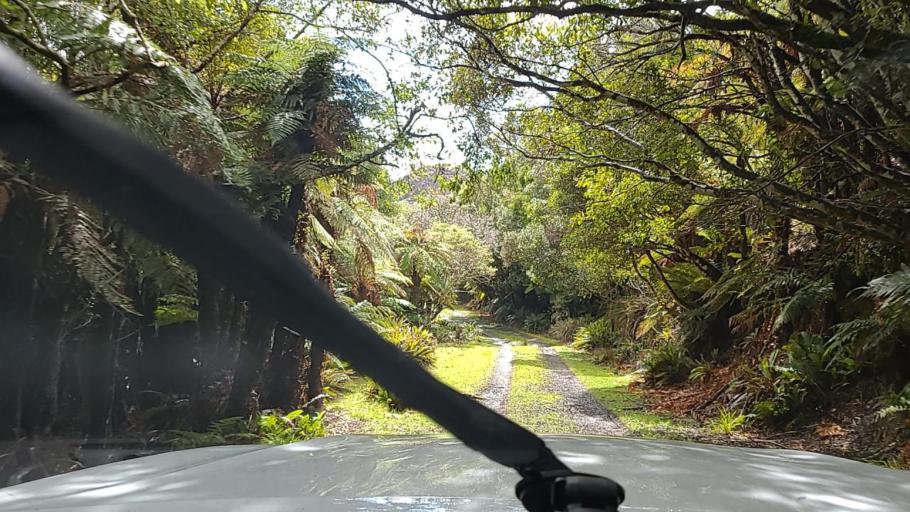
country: NZ
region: Bay of Plenty
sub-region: Opotiki District
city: Opotiki
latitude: -38.2017
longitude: 177.6195
